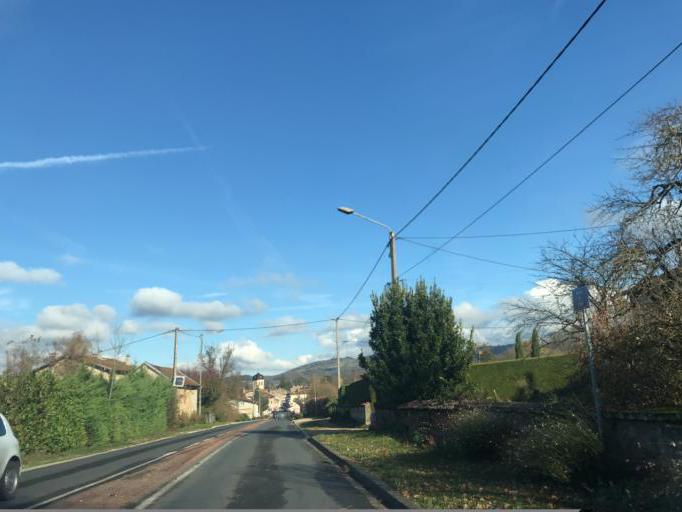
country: FR
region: Rhone-Alpes
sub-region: Departement de l'Ain
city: Saint-Jean-le-Vieux
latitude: 46.0252
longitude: 5.3840
